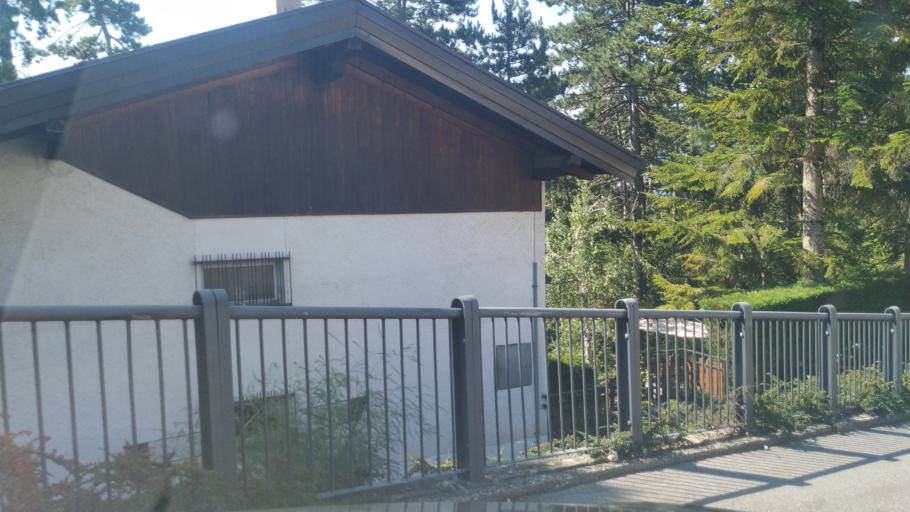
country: IT
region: Trentino-Alto Adige
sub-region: Provincia di Trento
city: Sanzeno
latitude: 46.3668
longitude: 11.0784
